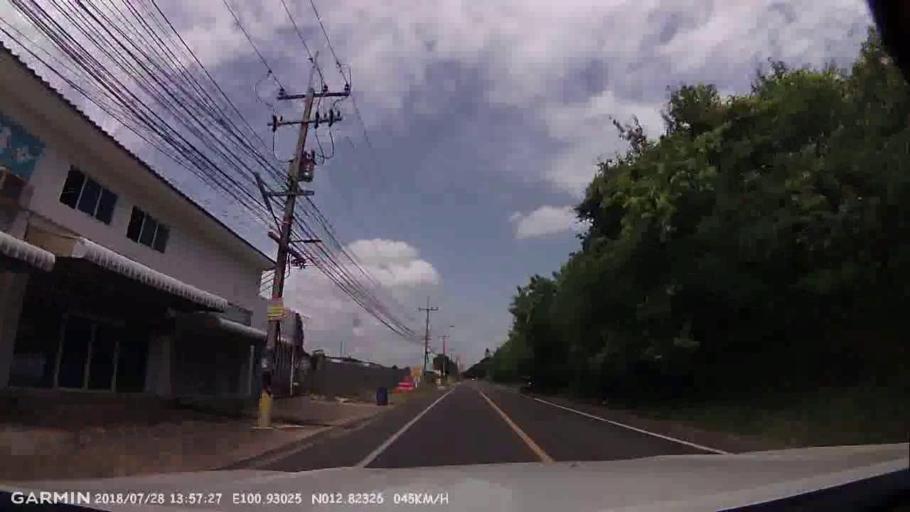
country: TH
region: Chon Buri
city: Phatthaya
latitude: 12.8233
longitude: 100.9301
